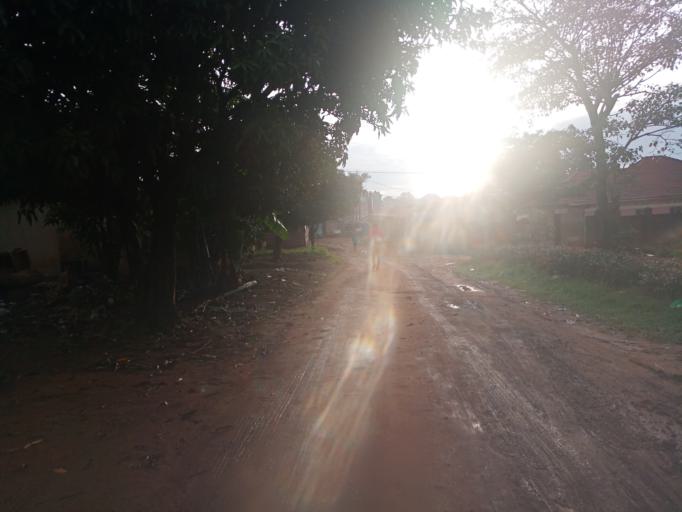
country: UG
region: Central Region
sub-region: Wakiso District
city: Kireka
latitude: 0.3925
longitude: 32.6363
